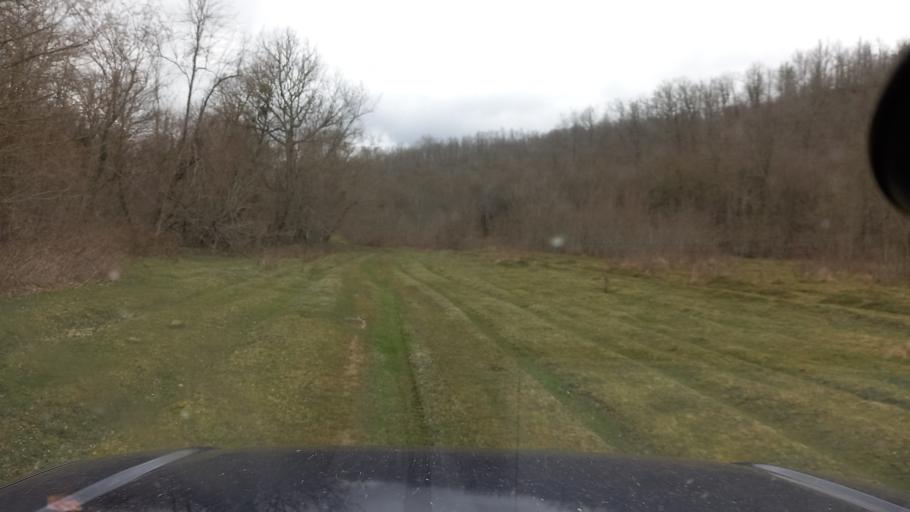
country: RU
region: Krasnodarskiy
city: Pshada
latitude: 44.4850
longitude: 38.4000
